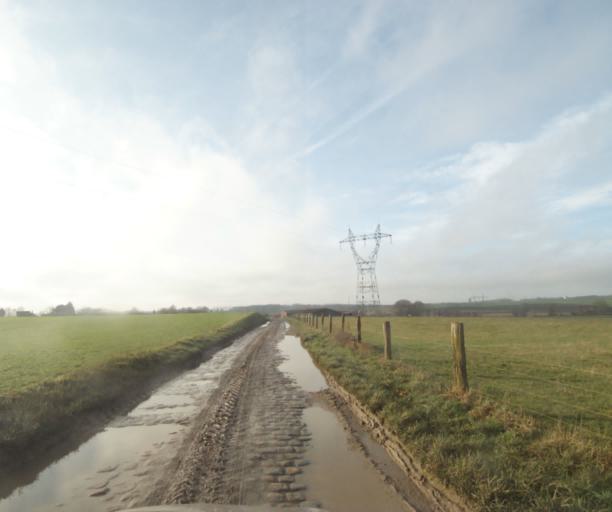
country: FR
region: Nord-Pas-de-Calais
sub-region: Departement du Nord
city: Thiant
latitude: 50.2937
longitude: 3.4604
